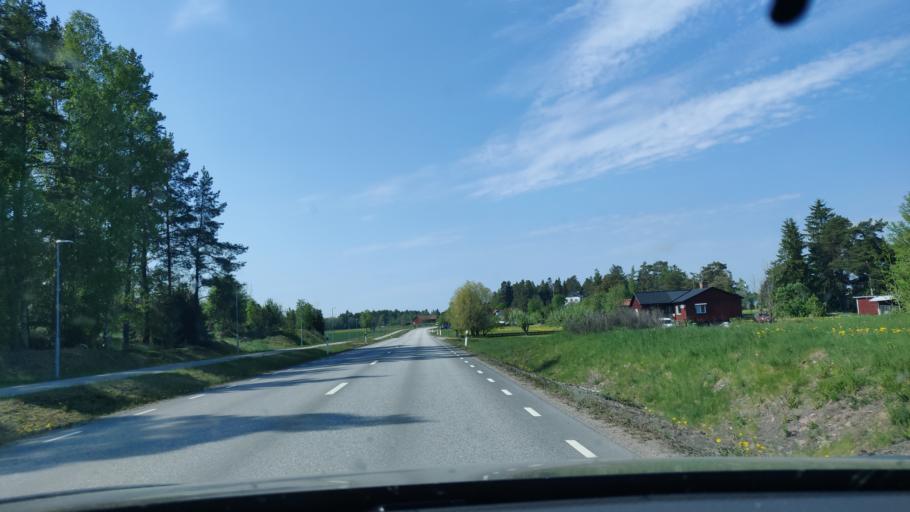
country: SE
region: Uppsala
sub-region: Heby Kommun
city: OEstervala
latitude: 60.1705
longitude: 17.1861
